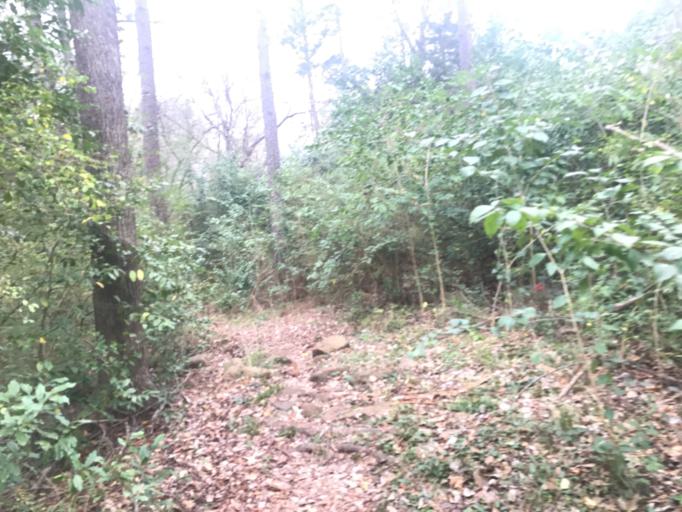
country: US
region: Texas
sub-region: Nacogdoches County
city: Nacogdoches
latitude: 31.6258
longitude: -94.6389
